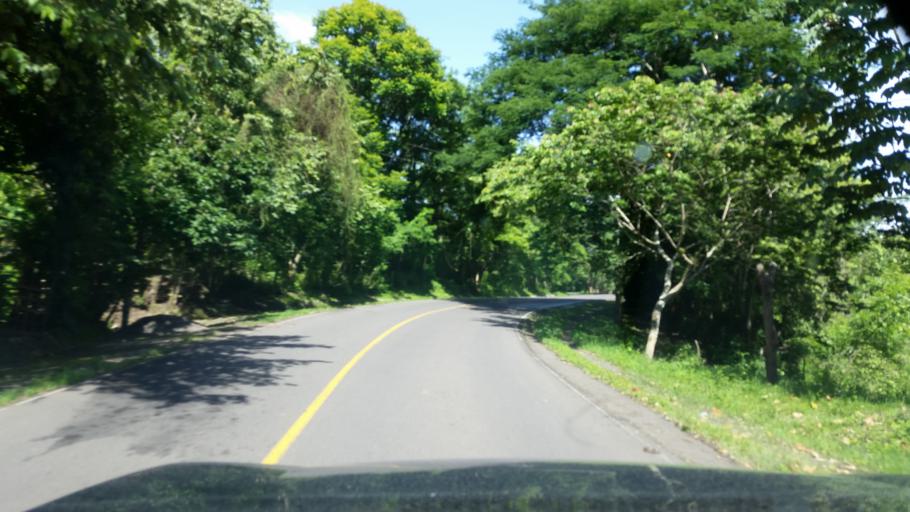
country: NI
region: Matagalpa
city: San Ramon
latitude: 13.0064
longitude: -85.7979
